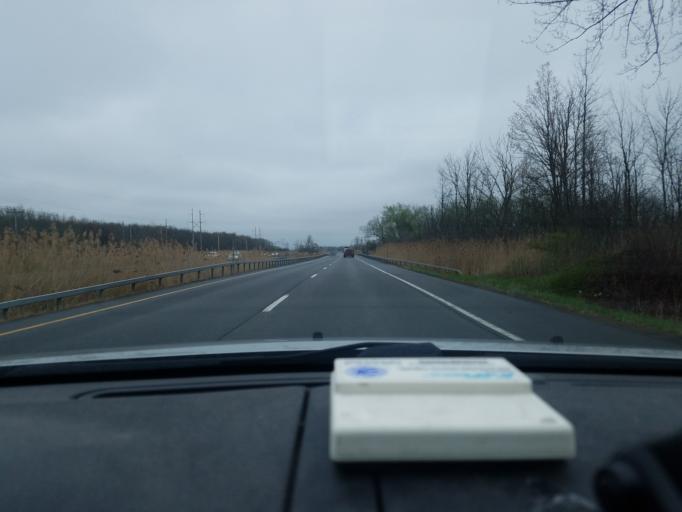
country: US
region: New York
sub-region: Onondaga County
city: East Syracuse
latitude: 43.1141
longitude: -76.0776
